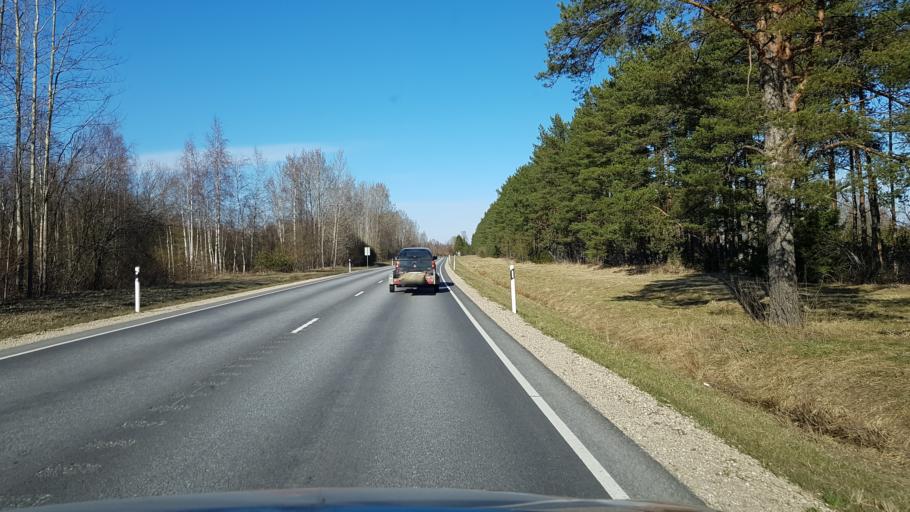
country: EE
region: Jogevamaa
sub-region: Mustvee linn
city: Mustvee
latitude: 58.9322
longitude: 27.0265
